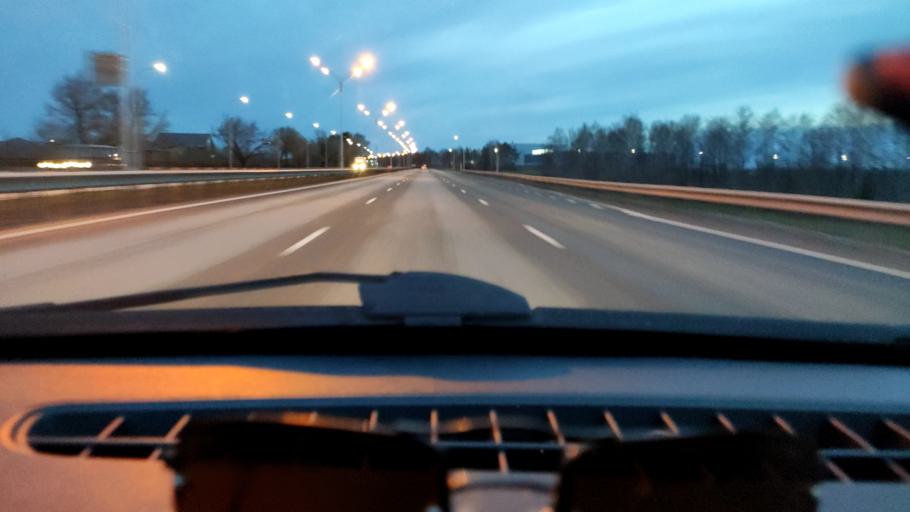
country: RU
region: Bashkortostan
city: Ufa
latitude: 54.6038
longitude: 55.9173
